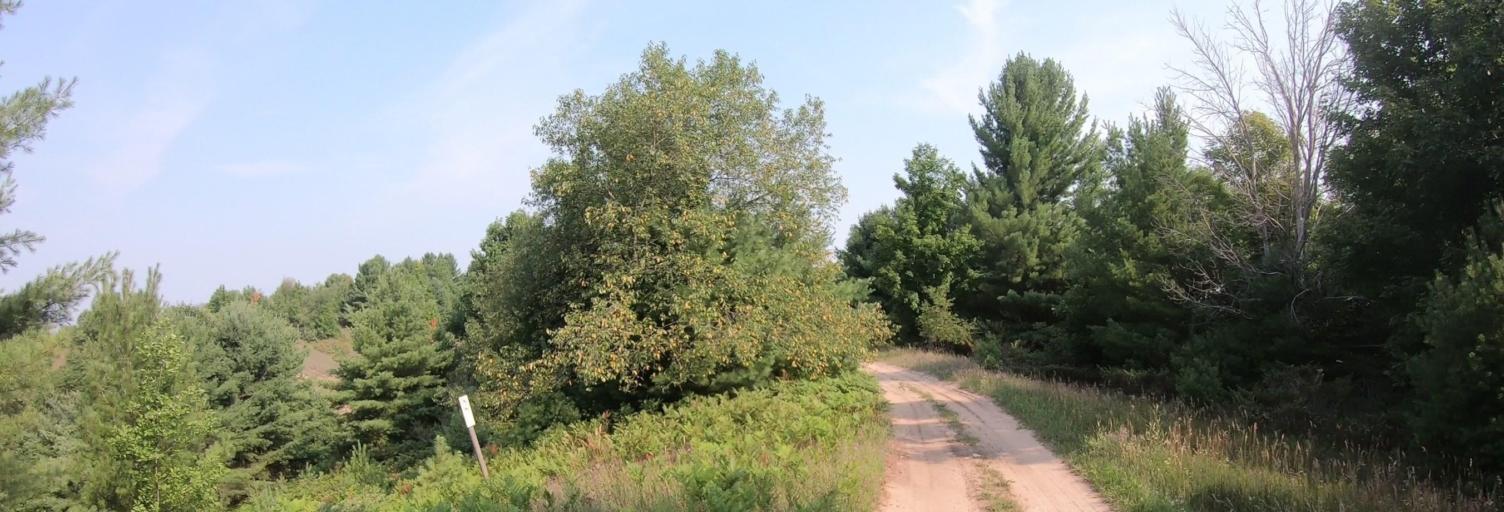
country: US
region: Michigan
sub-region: Benzie County
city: Beulah
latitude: 44.7616
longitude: -85.9261
